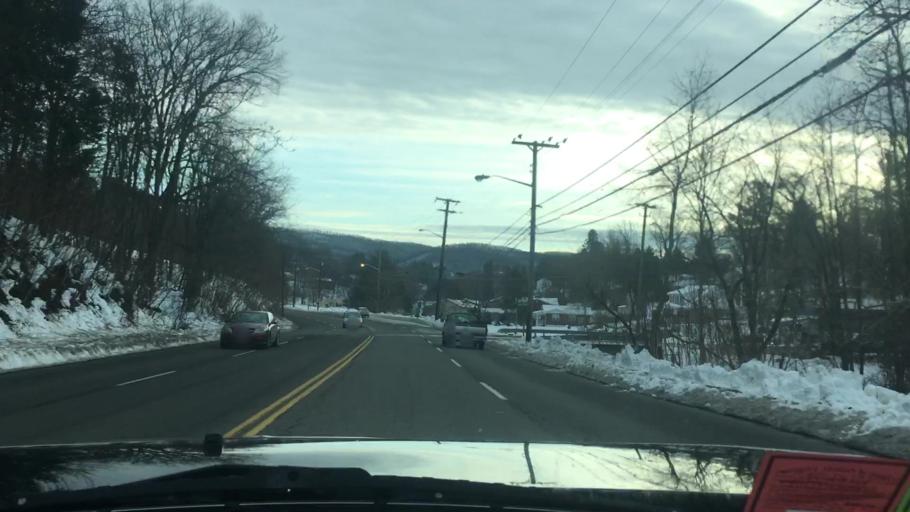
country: US
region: Virginia
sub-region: Pulaski County
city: Pulaski
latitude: 37.0607
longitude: -80.7720
